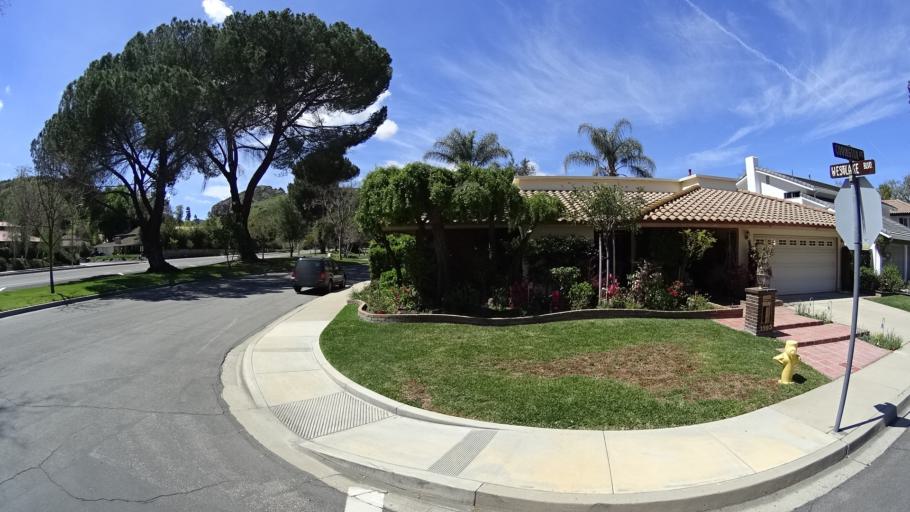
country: US
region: California
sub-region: Ventura County
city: Thousand Oaks
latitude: 34.1447
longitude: -118.8474
